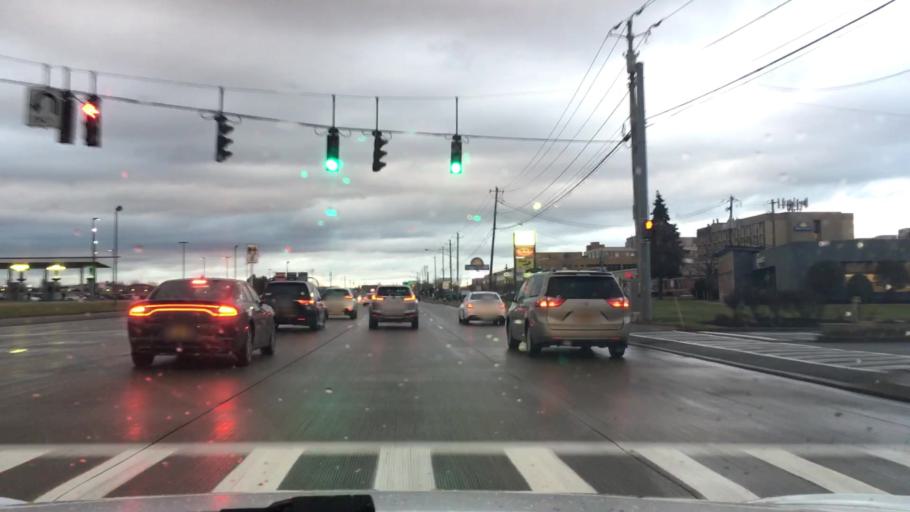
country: US
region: New York
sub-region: Erie County
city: Williamsville
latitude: 42.9325
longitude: -78.7280
